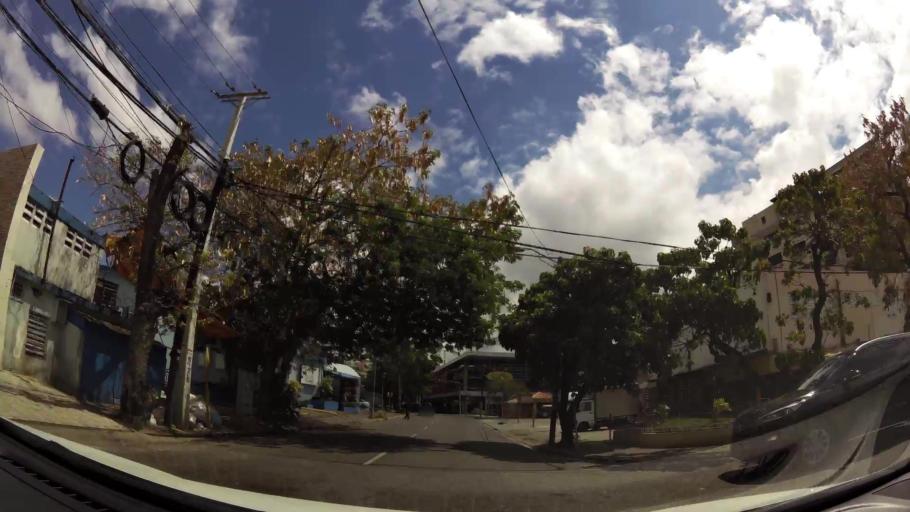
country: DO
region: Nacional
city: La Julia
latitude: 18.4725
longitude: -69.9263
